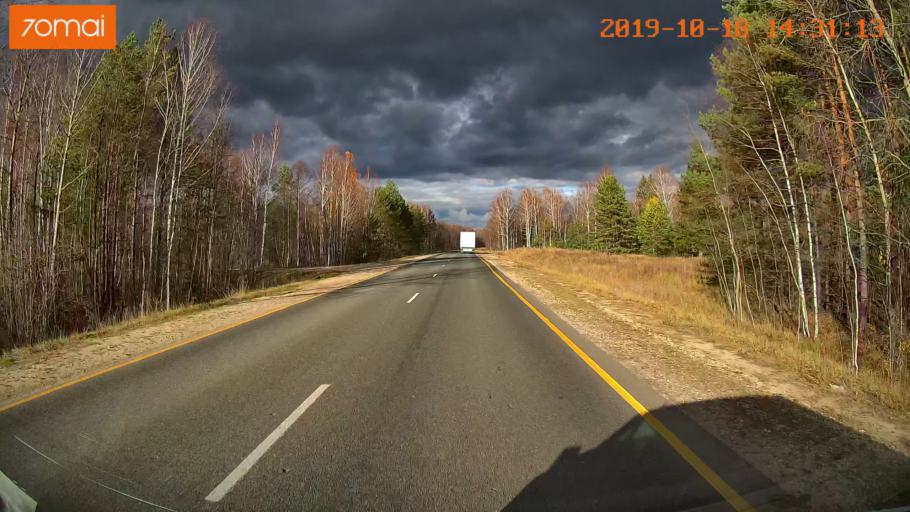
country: RU
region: Rjazan
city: Tuma
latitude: 55.1798
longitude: 40.5690
